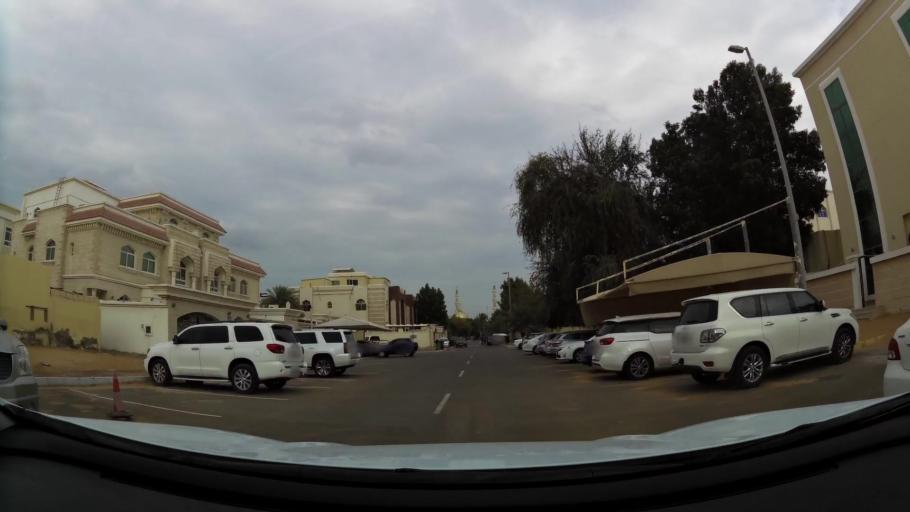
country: AE
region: Abu Dhabi
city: Abu Dhabi
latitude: 24.4414
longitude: 54.3923
